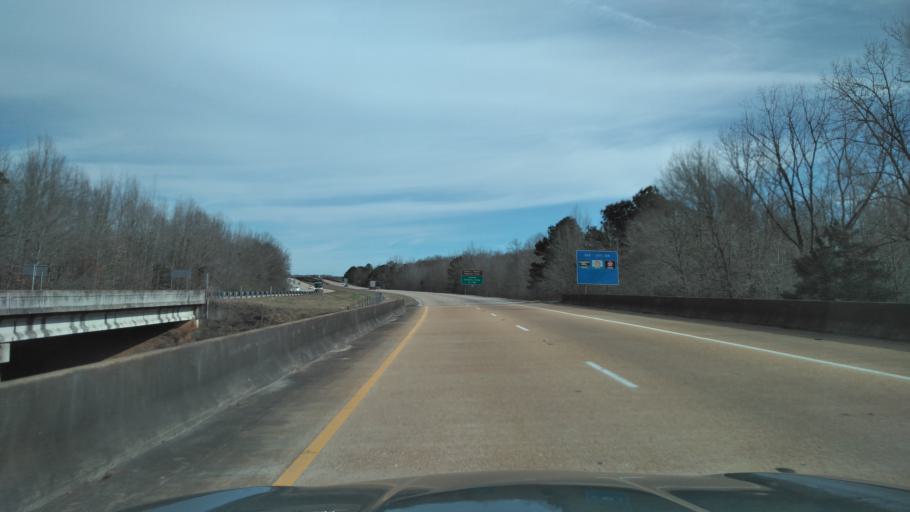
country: US
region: Mississippi
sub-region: Itawamba County
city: Fulton
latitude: 34.2324
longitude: -88.4216
